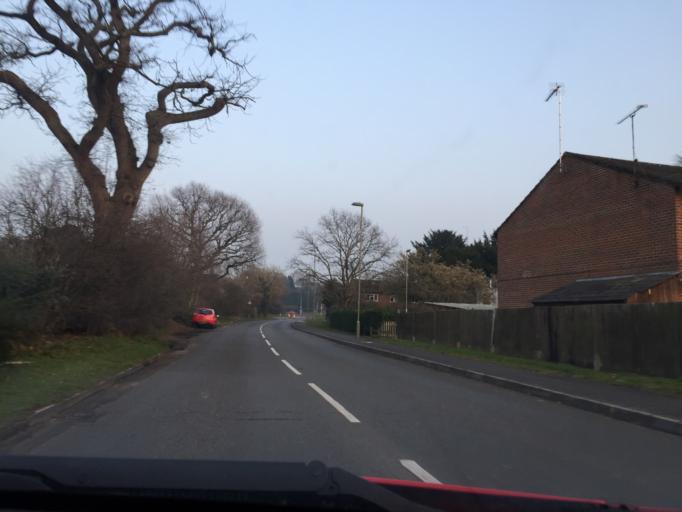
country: GB
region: England
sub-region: Hampshire
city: Ringwood
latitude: 50.8505
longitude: -1.7690
